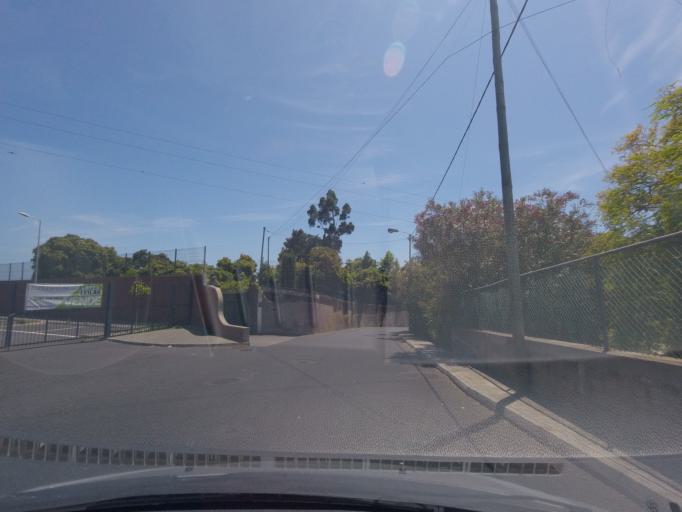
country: PT
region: Madeira
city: Camara de Lobos
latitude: 32.6470
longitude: -16.9573
